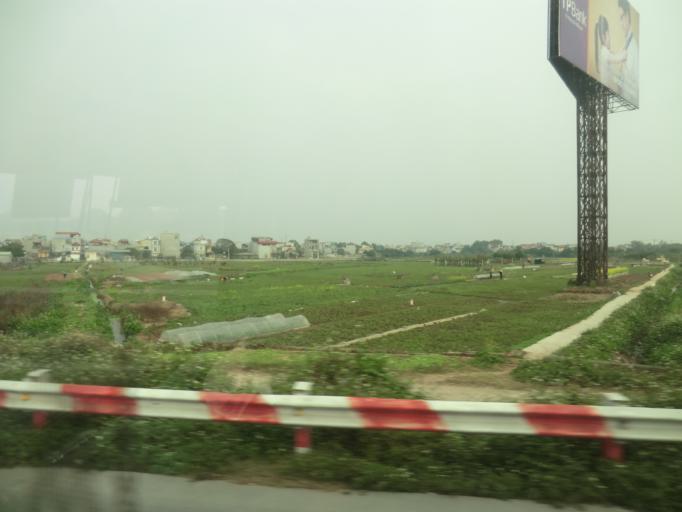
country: VN
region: Ha Noi
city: Van Dien
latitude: 20.9153
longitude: 105.8600
